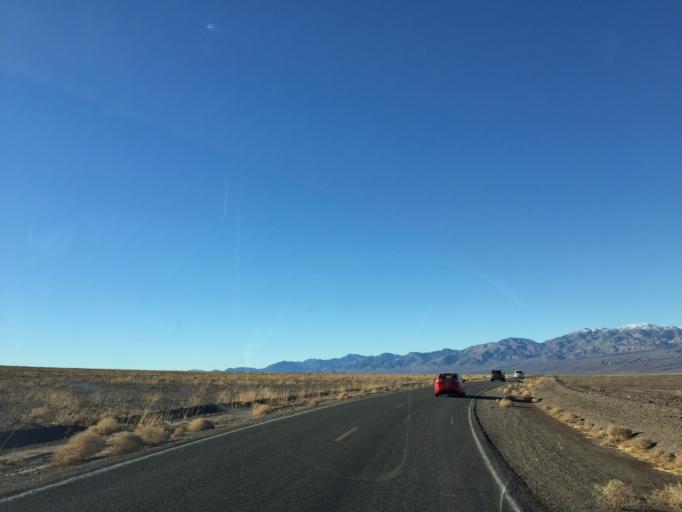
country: US
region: California
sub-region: San Bernardino County
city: Searles Valley
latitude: 36.1387
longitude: -116.7653
